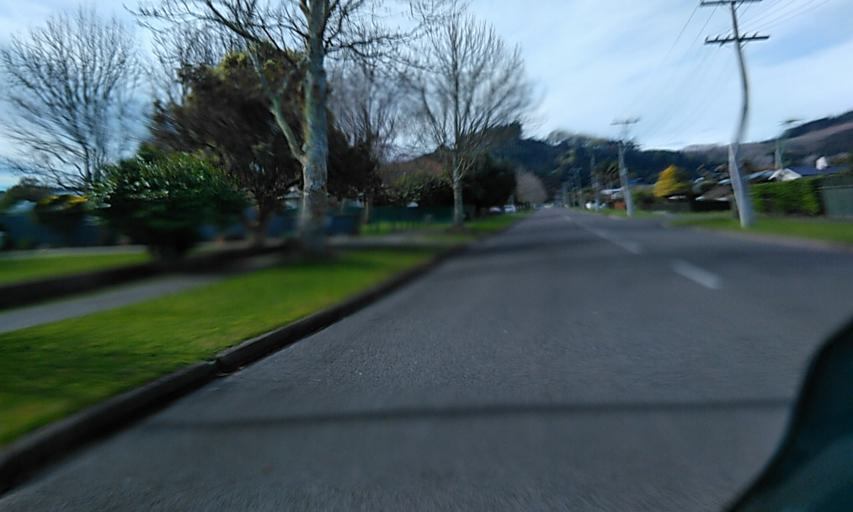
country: NZ
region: Gisborne
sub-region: Gisborne District
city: Gisborne
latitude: -38.6403
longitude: 178.0081
